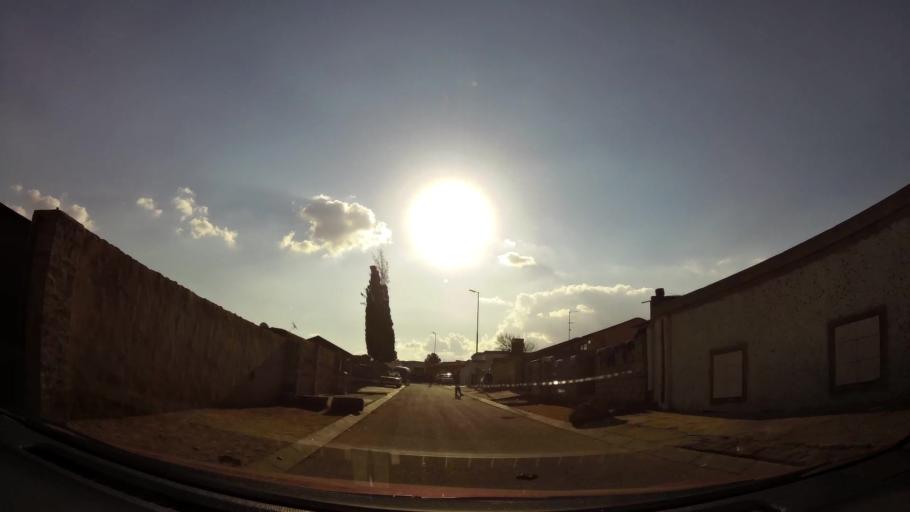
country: ZA
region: Gauteng
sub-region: City of Johannesburg Metropolitan Municipality
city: Soweto
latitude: -26.2337
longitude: 27.8619
